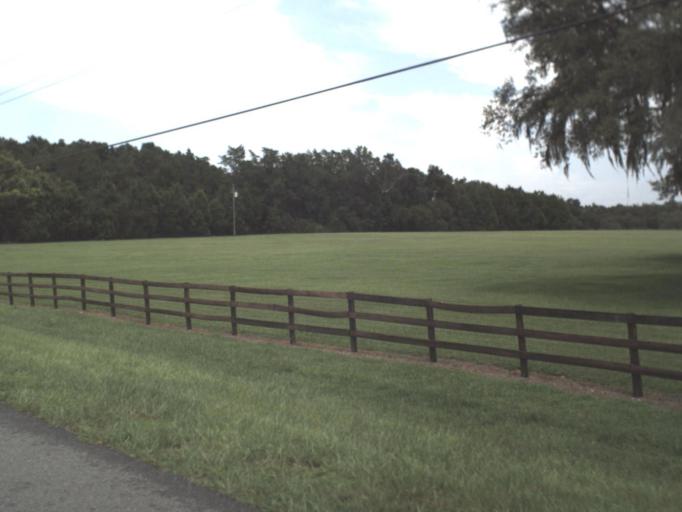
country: US
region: Florida
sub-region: Hernando County
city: Ridge Manor
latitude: 28.4878
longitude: -82.1960
